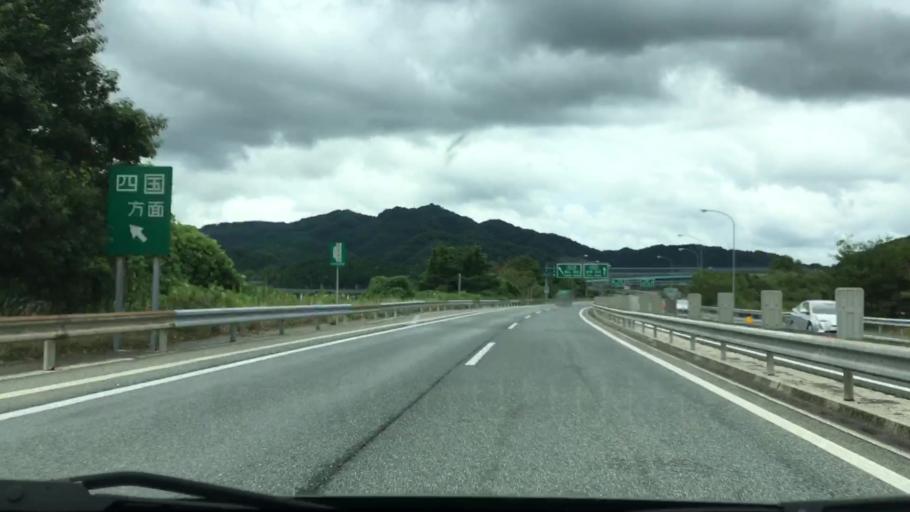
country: JP
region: Okayama
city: Takahashi
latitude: 34.9874
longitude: 133.6879
